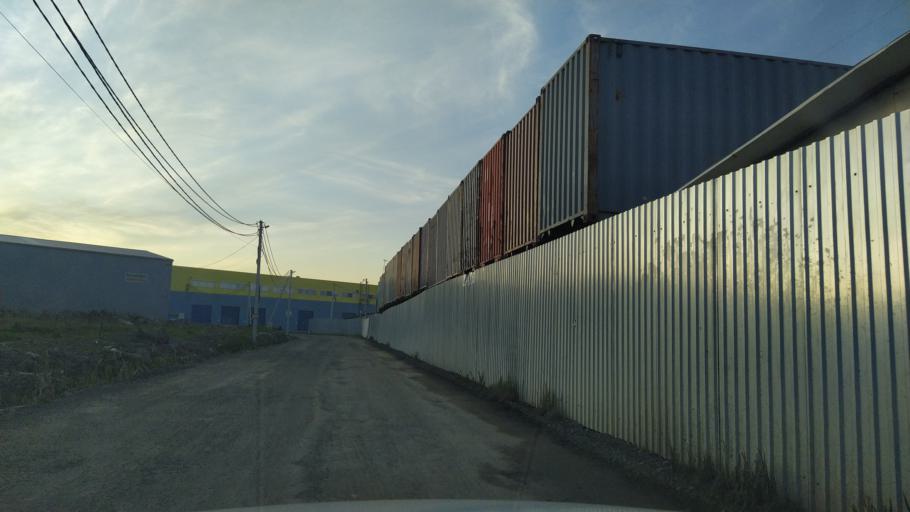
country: RU
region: St.-Petersburg
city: Obukhovo
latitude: 59.8052
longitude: 30.4596
